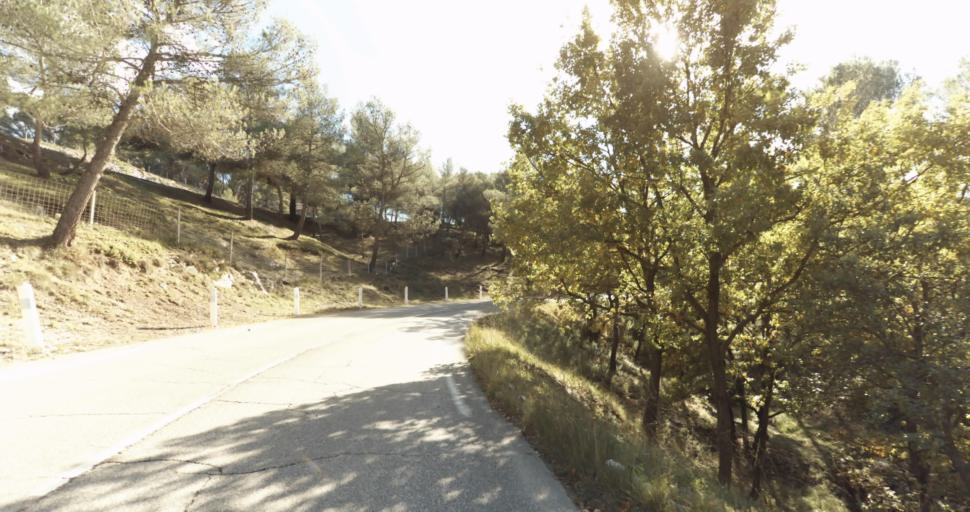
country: FR
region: Provence-Alpes-Cote d'Azur
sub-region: Departement des Bouches-du-Rhone
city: Venelles
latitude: 43.6041
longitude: 5.4962
